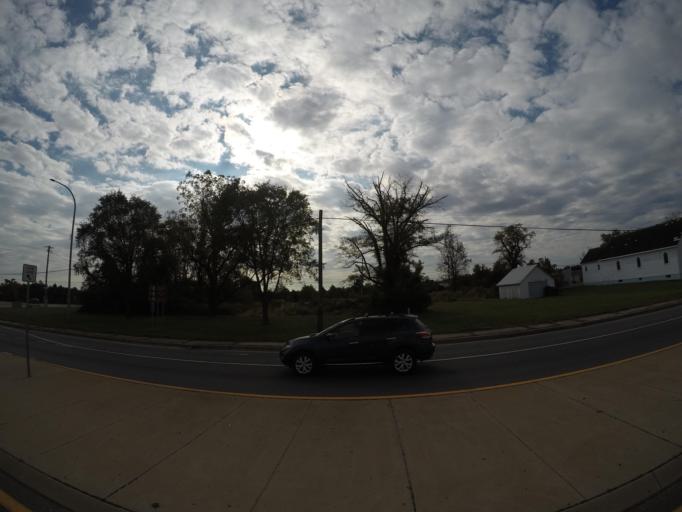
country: US
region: Delaware
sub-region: Sussex County
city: Lewes
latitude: 38.7472
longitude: -75.1771
